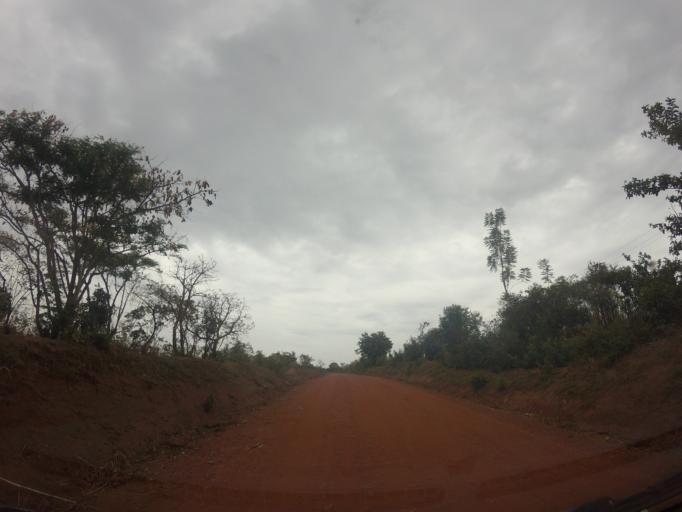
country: UG
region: Northern Region
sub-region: Arua District
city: Arua
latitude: 2.7697
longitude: 30.8597
